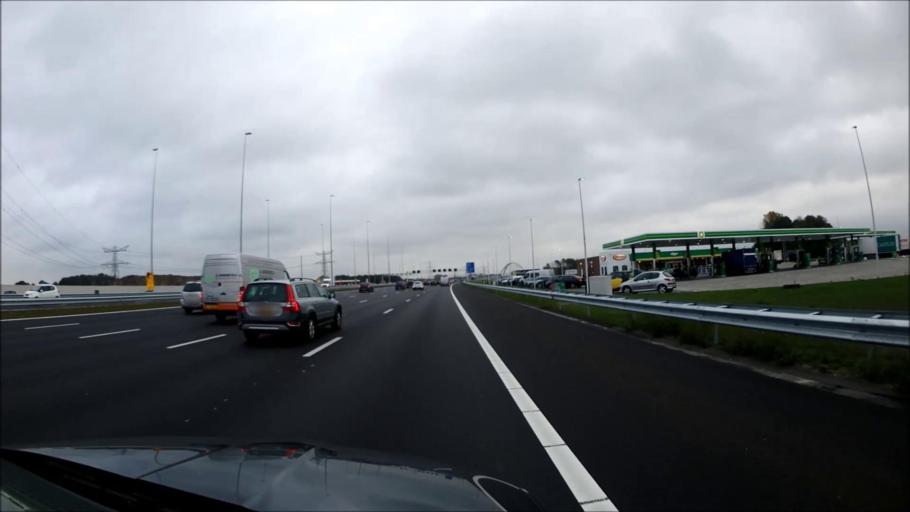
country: NL
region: North Holland
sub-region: Gemeente Weesp
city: Weesp
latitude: 52.3213
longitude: 5.0770
